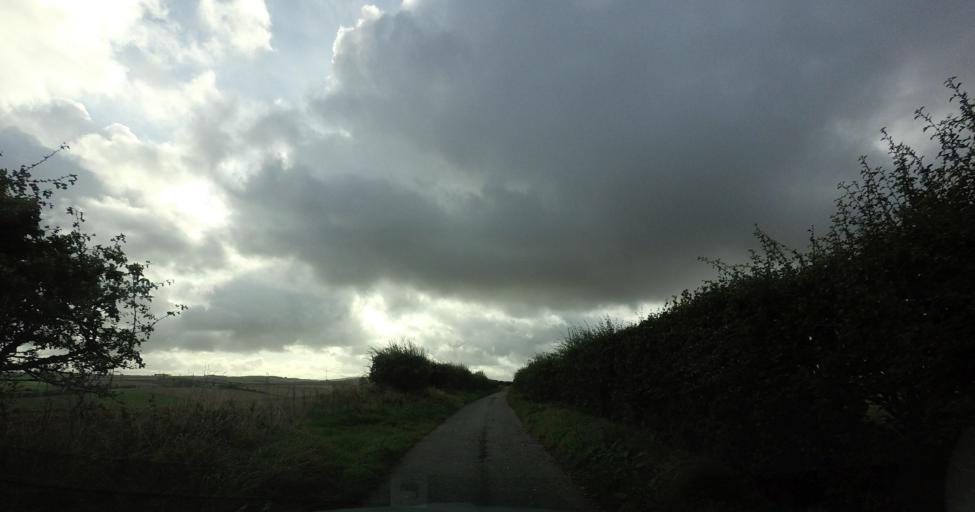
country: GB
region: Scotland
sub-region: Aberdeenshire
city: Whitehills
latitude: 57.6611
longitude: -2.6078
